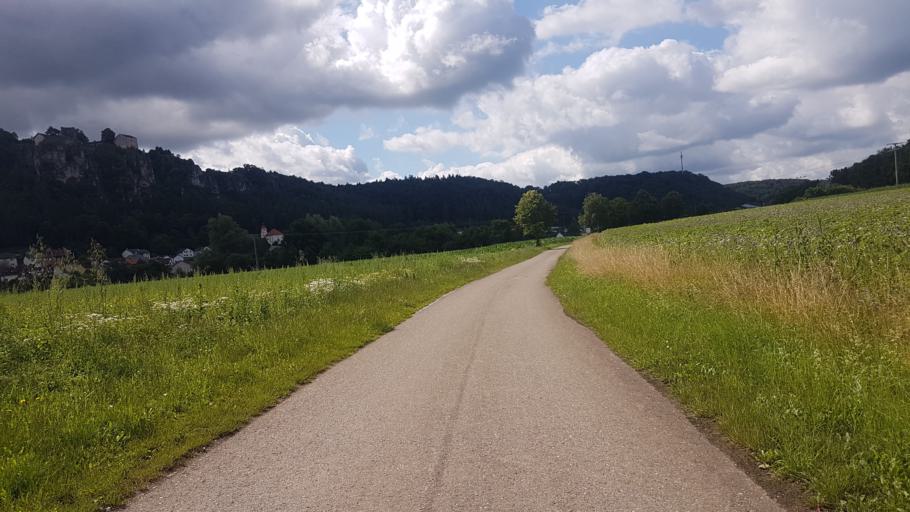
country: DE
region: Bavaria
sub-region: Upper Bavaria
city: Bohmfeld
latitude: 48.9318
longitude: 11.3722
